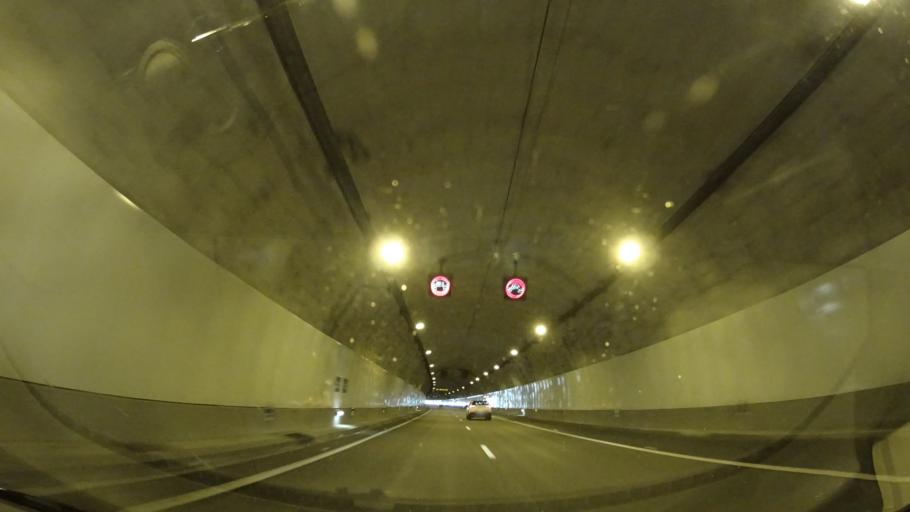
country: ES
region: Andalusia
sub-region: Provincia de Sevilla
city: El Ronquillo
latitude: 37.6465
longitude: -6.1573
